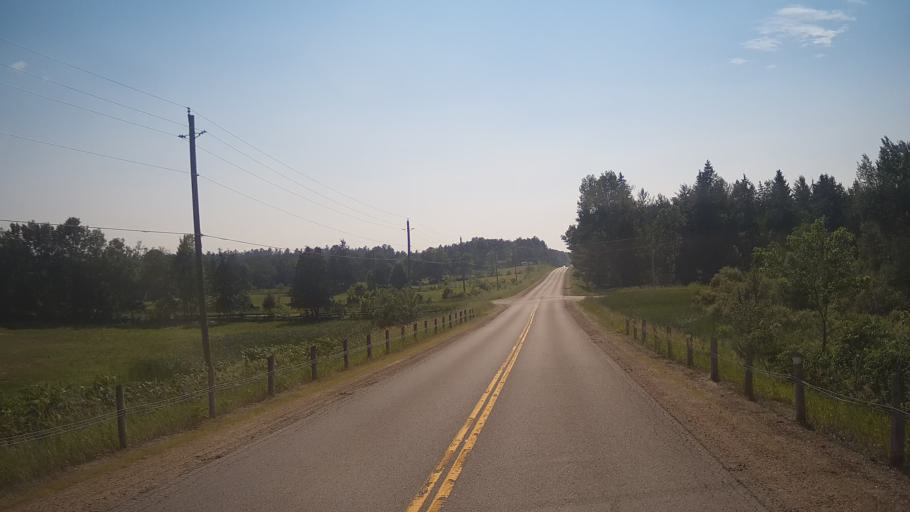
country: CA
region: Ontario
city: Pembroke
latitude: 45.6103
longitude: -77.2037
